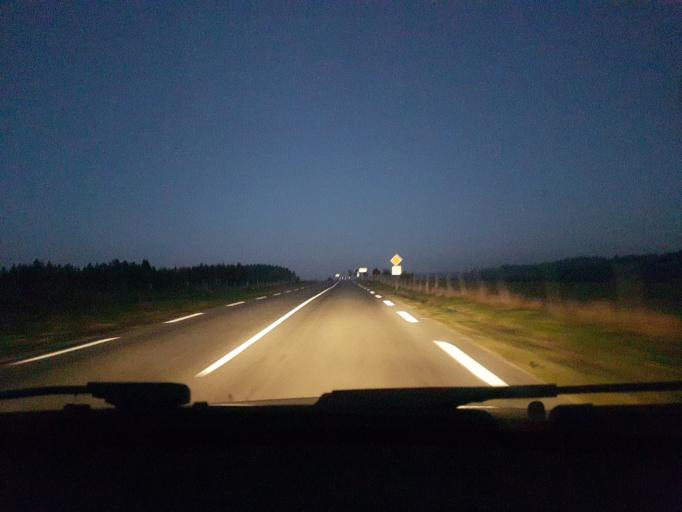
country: CH
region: Neuchatel
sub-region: Le Locle District
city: Les Brenets
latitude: 47.1110
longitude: 6.6891
